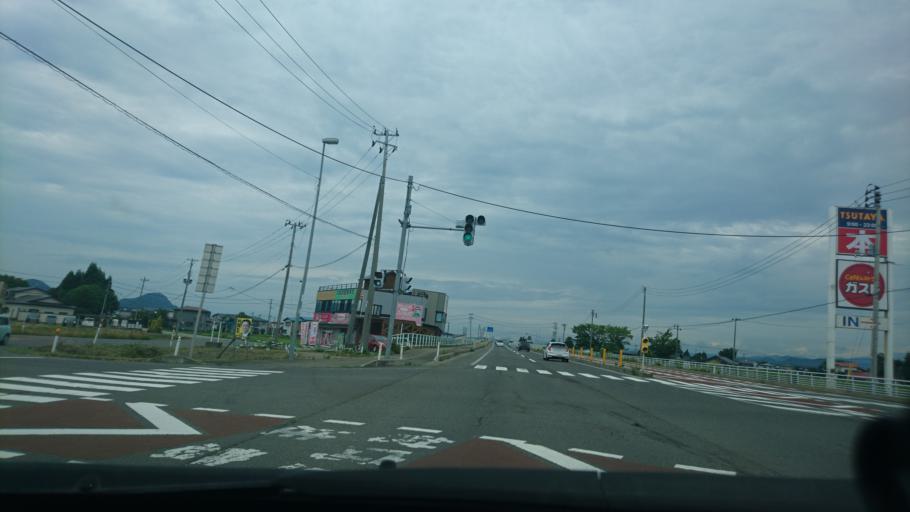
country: JP
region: Akita
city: Omagari
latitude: 39.4580
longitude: 140.4957
